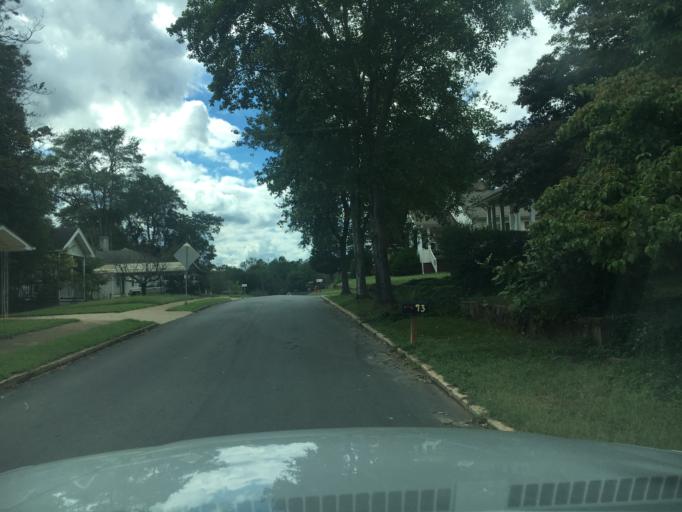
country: US
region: South Carolina
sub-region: Spartanburg County
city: Lyman
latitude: 34.9470
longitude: -82.1318
